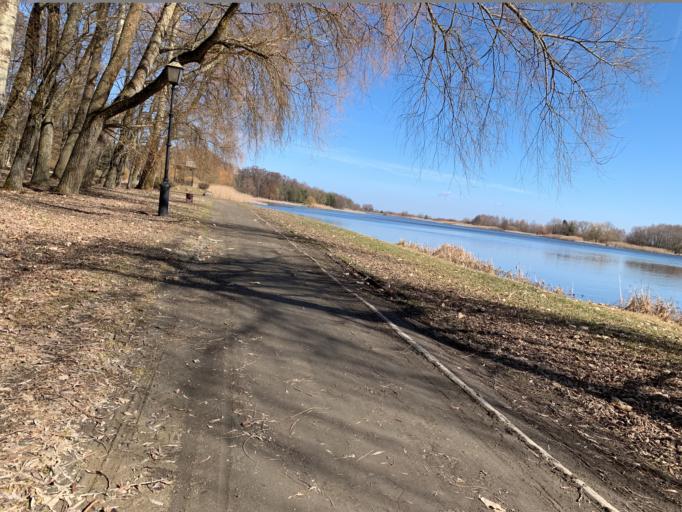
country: BY
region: Minsk
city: Nyasvizh
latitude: 53.2273
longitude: 26.6972
